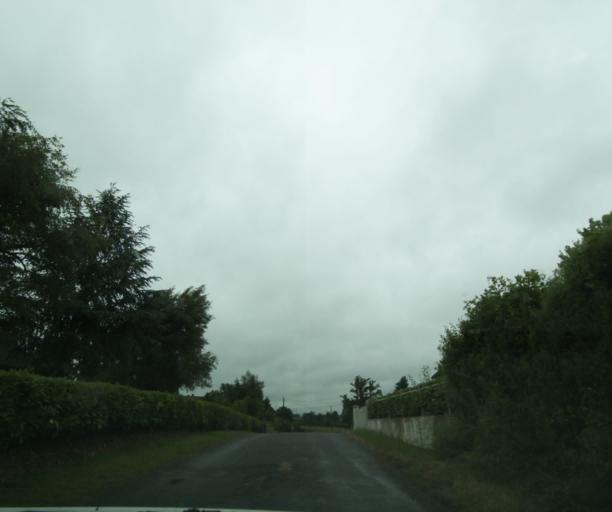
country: FR
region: Bourgogne
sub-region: Departement de Saone-et-Loire
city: Genelard
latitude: 46.5768
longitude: 4.2166
